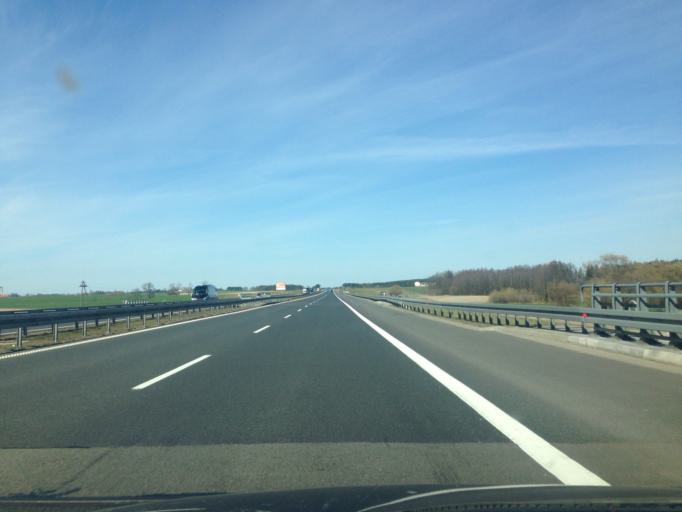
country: PL
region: Pomeranian Voivodeship
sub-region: Powiat starogardzki
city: Smetowo Graniczne
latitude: 53.7680
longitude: 18.6340
